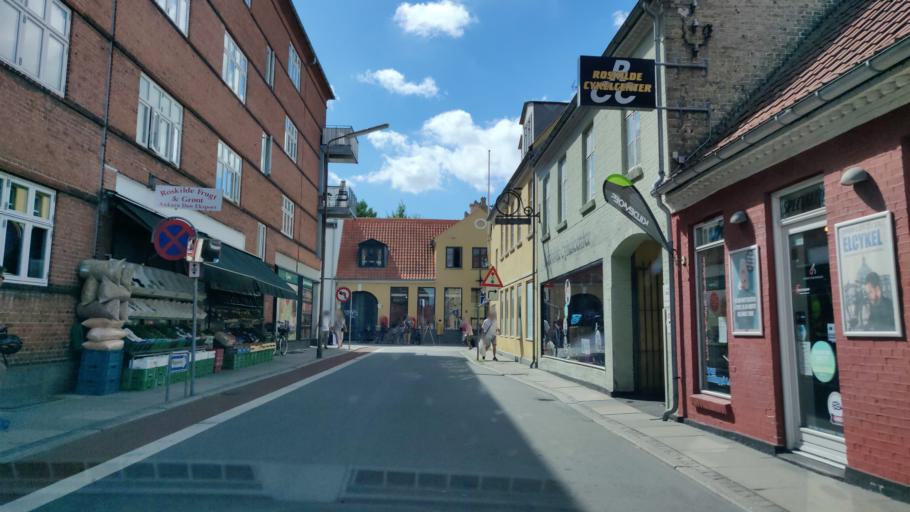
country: DK
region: Zealand
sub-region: Roskilde Kommune
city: Roskilde
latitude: 55.6411
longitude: 12.0760
